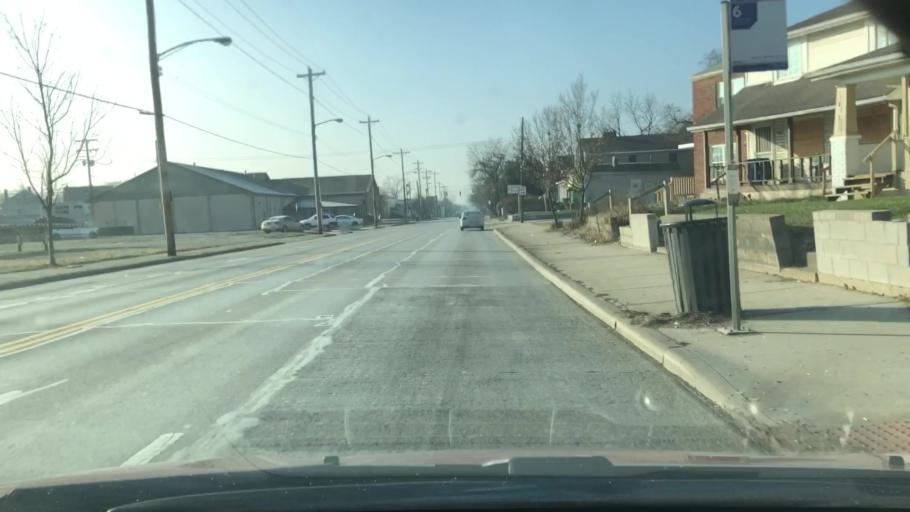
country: US
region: Ohio
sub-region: Franklin County
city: Bexley
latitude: 40.0046
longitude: -82.9730
